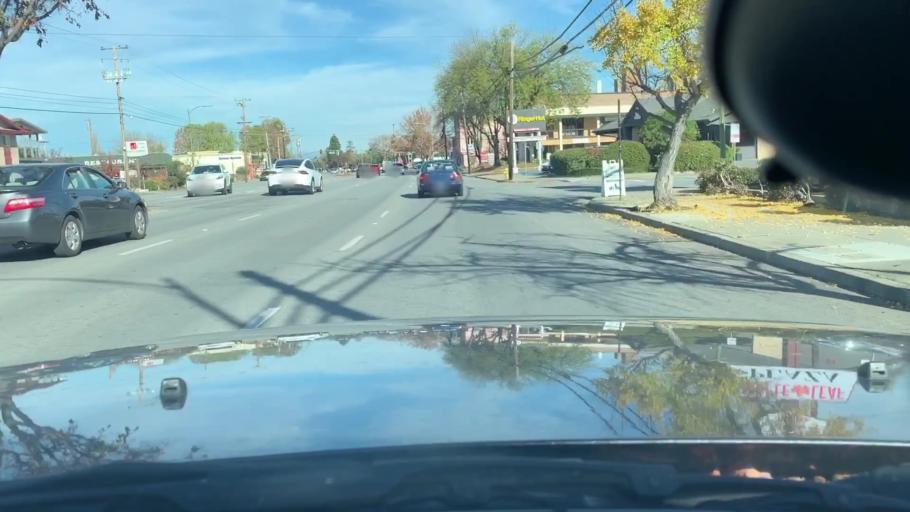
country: US
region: California
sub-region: Santa Clara County
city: Campbell
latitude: 37.3061
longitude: -121.9781
